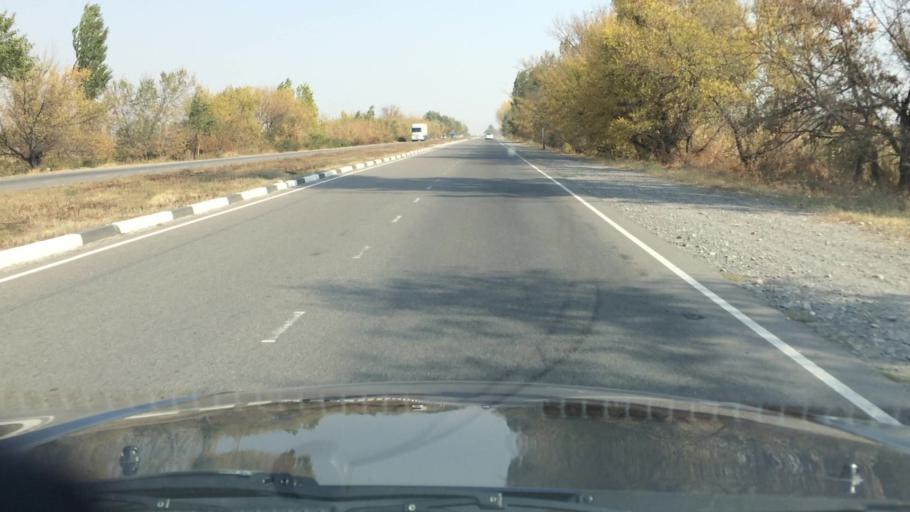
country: KG
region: Chuy
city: Kant
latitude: 42.9517
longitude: 74.7878
